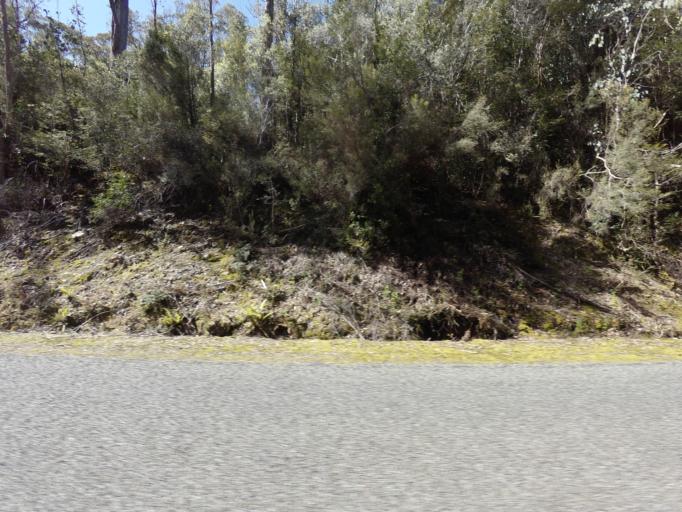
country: AU
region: Tasmania
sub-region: Derwent Valley
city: New Norfolk
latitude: -42.7369
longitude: 146.4232
